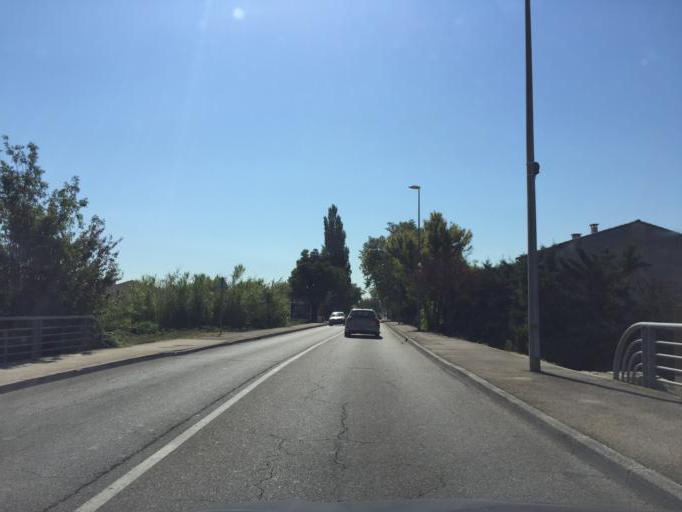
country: FR
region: Provence-Alpes-Cote d'Azur
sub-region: Departement du Vaucluse
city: Vedene
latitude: 43.9822
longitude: 4.9043
